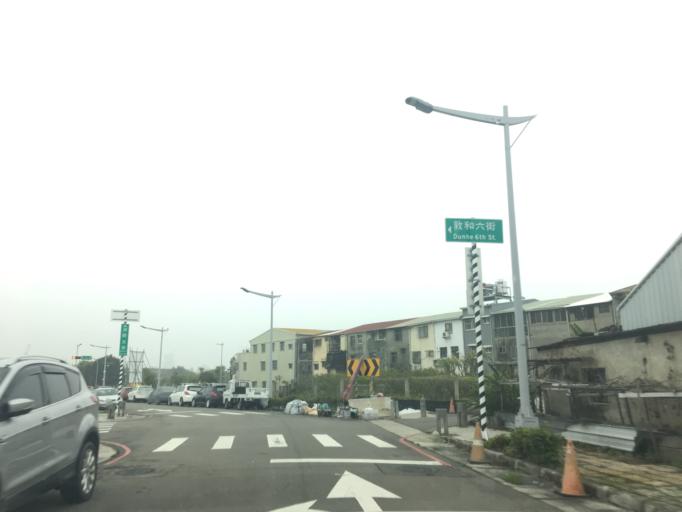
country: TW
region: Taiwan
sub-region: Taichung City
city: Taichung
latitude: 24.1942
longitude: 120.6721
